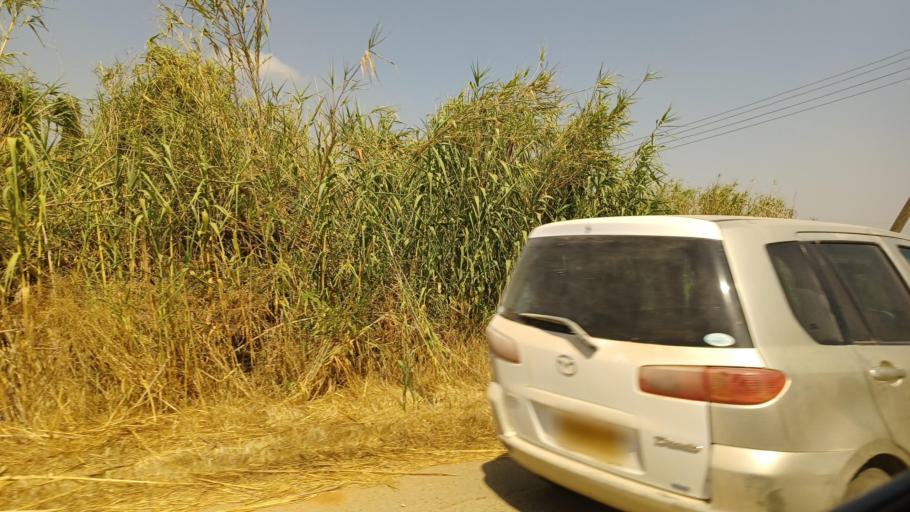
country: CY
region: Ammochostos
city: Frenaros
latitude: 35.0581
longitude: 33.9215
